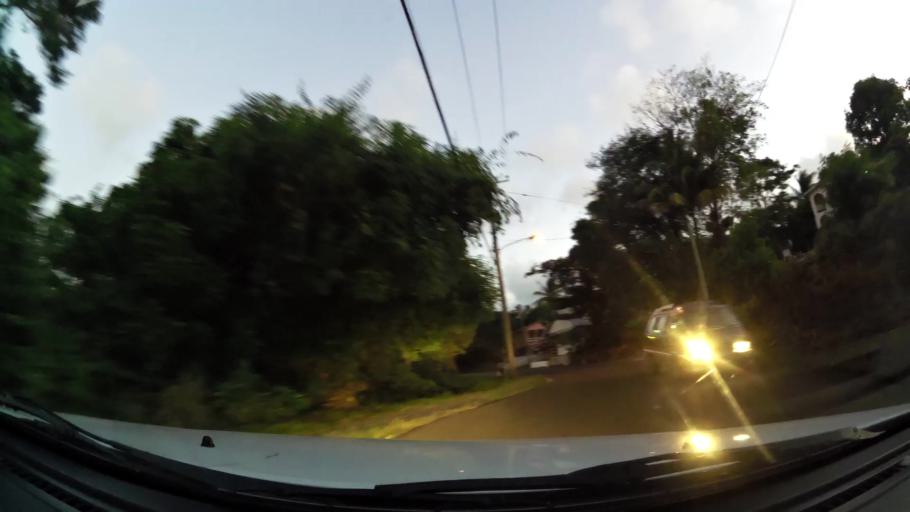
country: LC
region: Castries Quarter
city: Bisee
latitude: 14.0384
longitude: -60.9528
